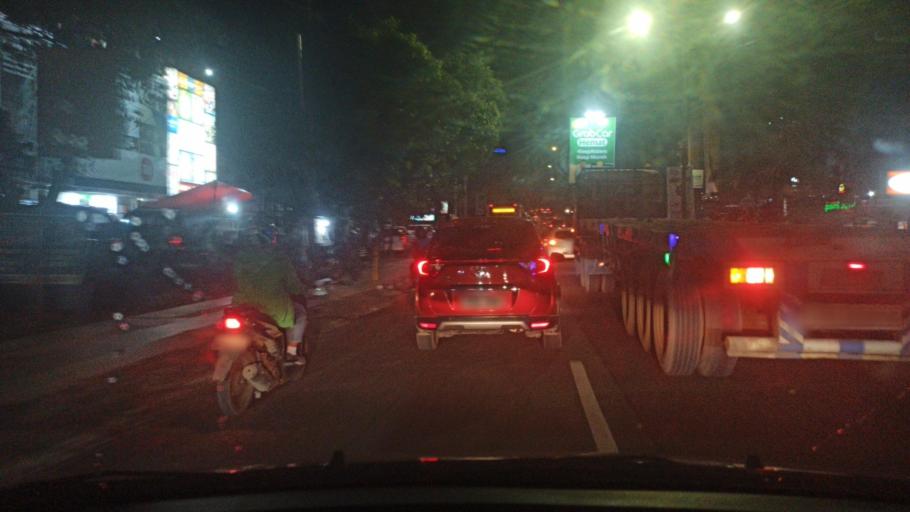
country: ID
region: South Sumatra
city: Palembang
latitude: -2.9568
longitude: 104.7437
